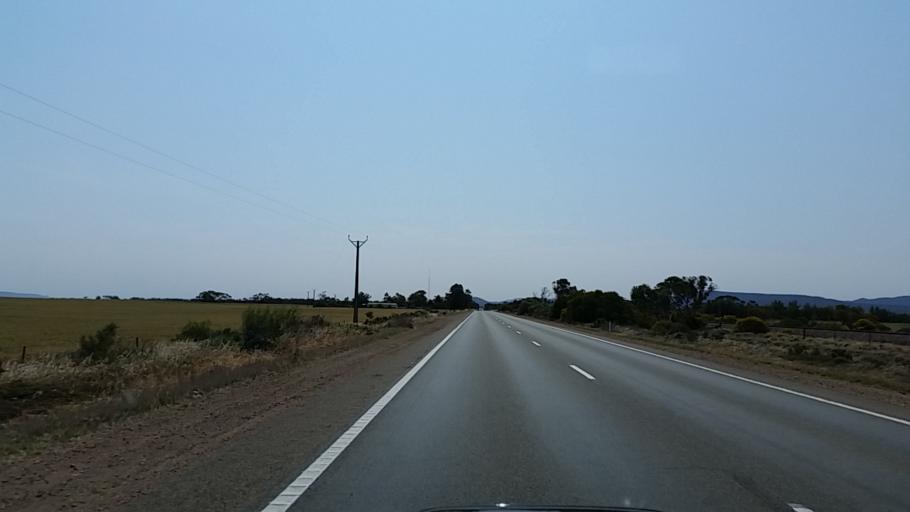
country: AU
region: South Australia
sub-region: Port Pirie City and Dists
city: Port Pirie
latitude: -32.9297
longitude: 137.9824
